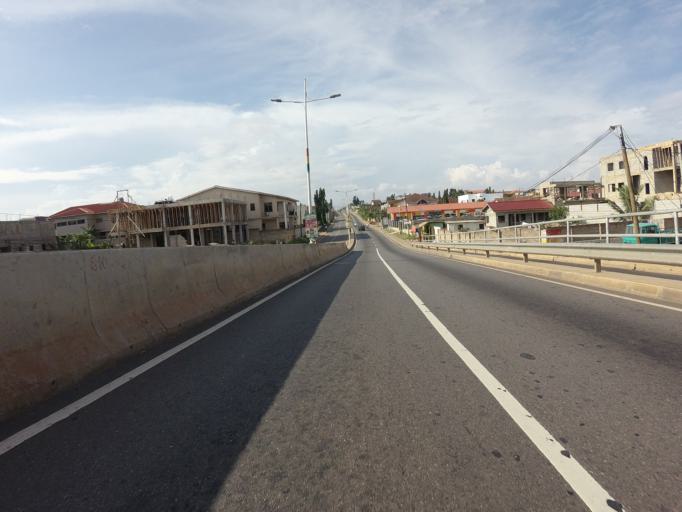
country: GH
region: Greater Accra
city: Medina Estates
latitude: 5.6205
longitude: -0.1527
